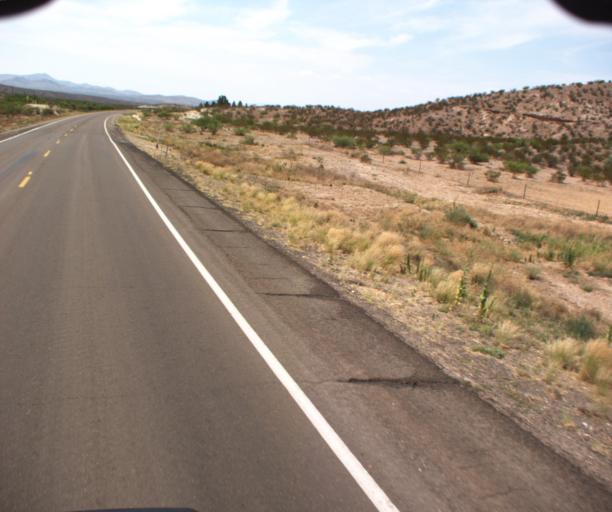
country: US
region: Arizona
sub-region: Greenlee County
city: Clifton
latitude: 32.7673
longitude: -109.1487
